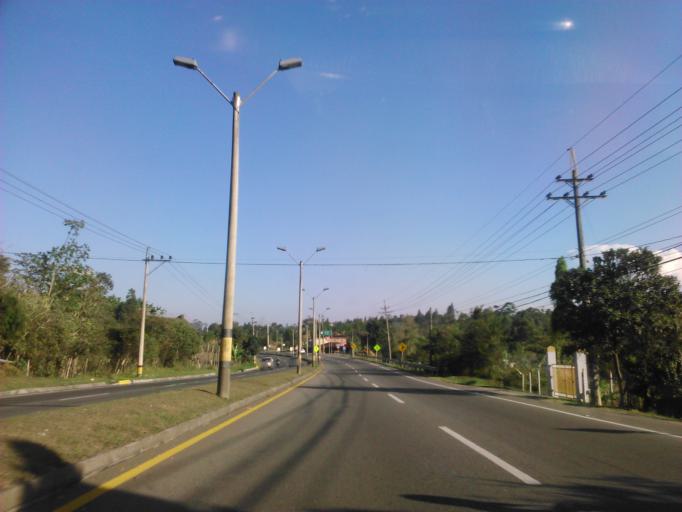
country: CO
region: Antioquia
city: Guarne
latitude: 6.2319
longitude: -75.4106
